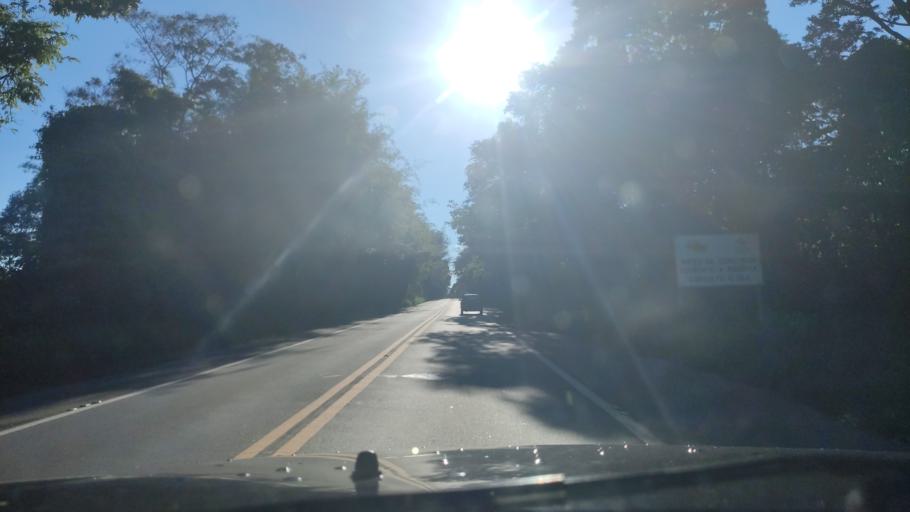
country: BR
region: Sao Paulo
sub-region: Socorro
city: Socorro
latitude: -22.5533
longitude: -46.5654
